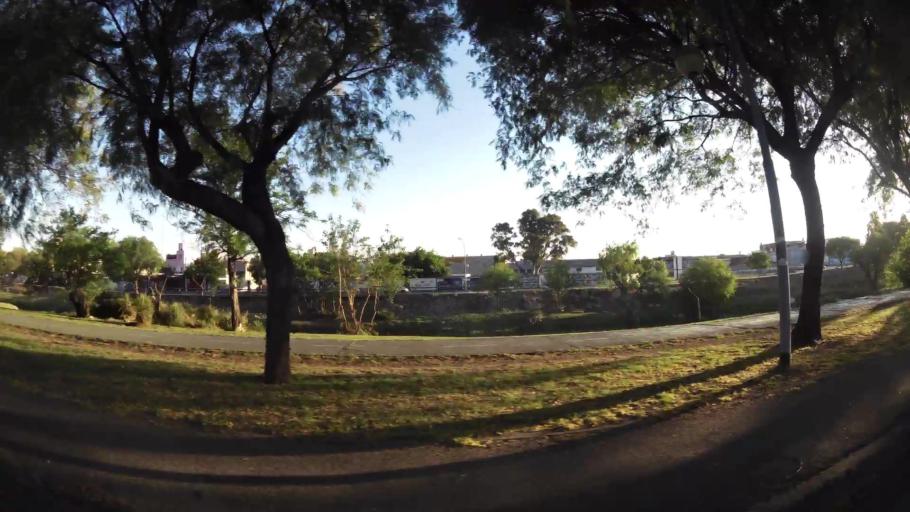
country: AR
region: Cordoba
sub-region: Departamento de Capital
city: Cordoba
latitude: -31.3911
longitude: -64.2087
